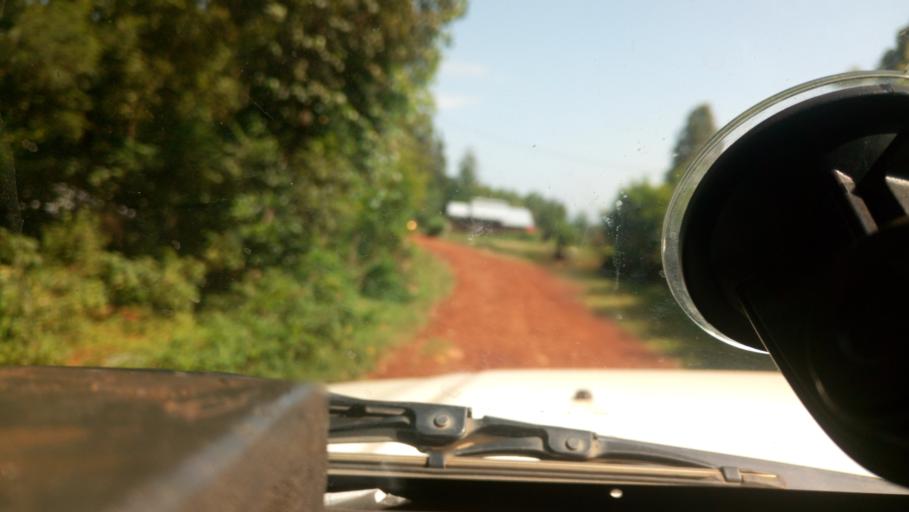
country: KE
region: Kisii
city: Ogembo
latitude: -0.7285
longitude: 34.7047
